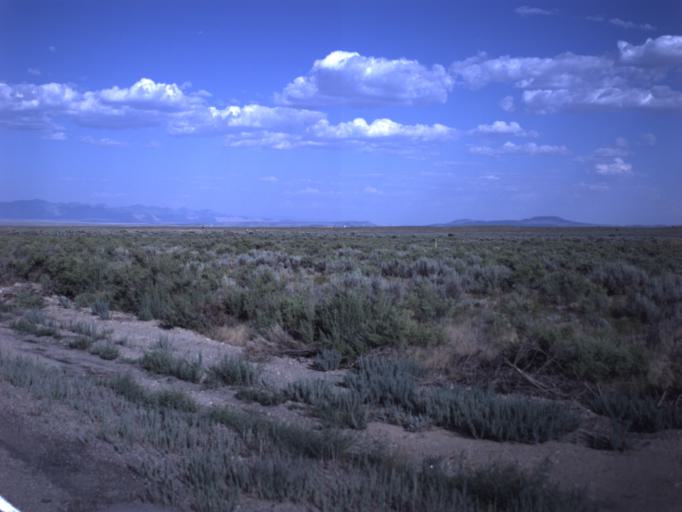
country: US
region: Utah
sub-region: Carbon County
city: Price
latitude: 39.4873
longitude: -110.8741
